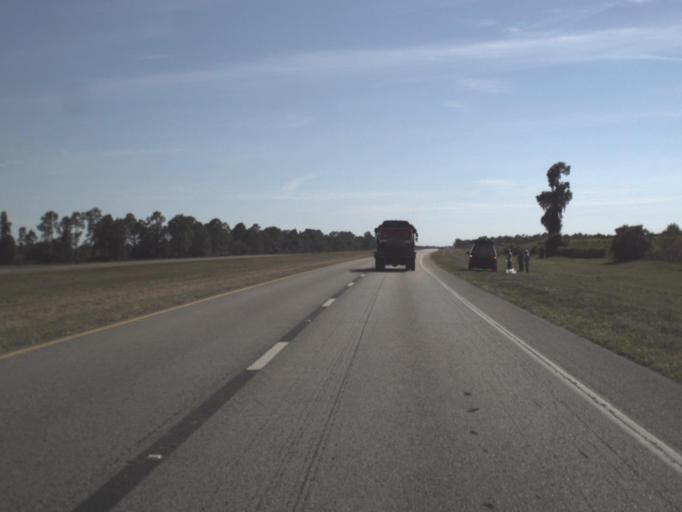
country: US
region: Florida
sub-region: Highlands County
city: Placid Lakes
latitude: 27.0787
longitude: -81.3352
